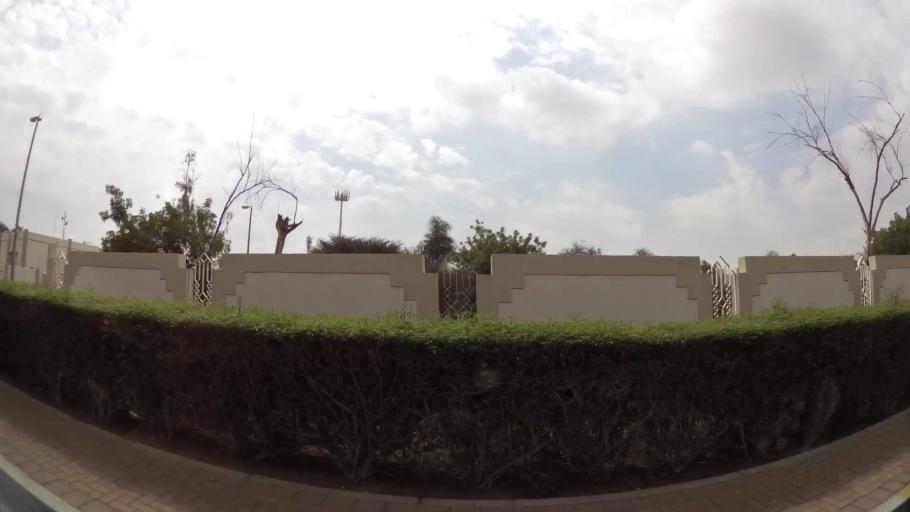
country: OM
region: Al Buraimi
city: Al Buraymi
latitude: 24.2252
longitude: 55.7712
